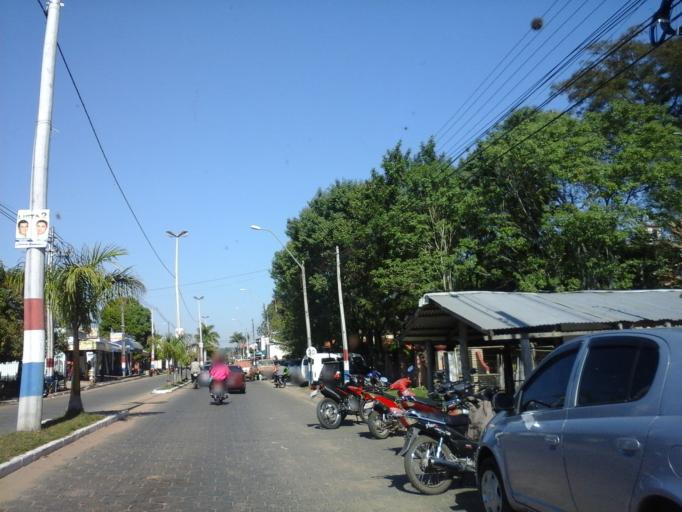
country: PY
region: Neembucu
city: Pilar
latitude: -26.8679
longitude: -58.3019
